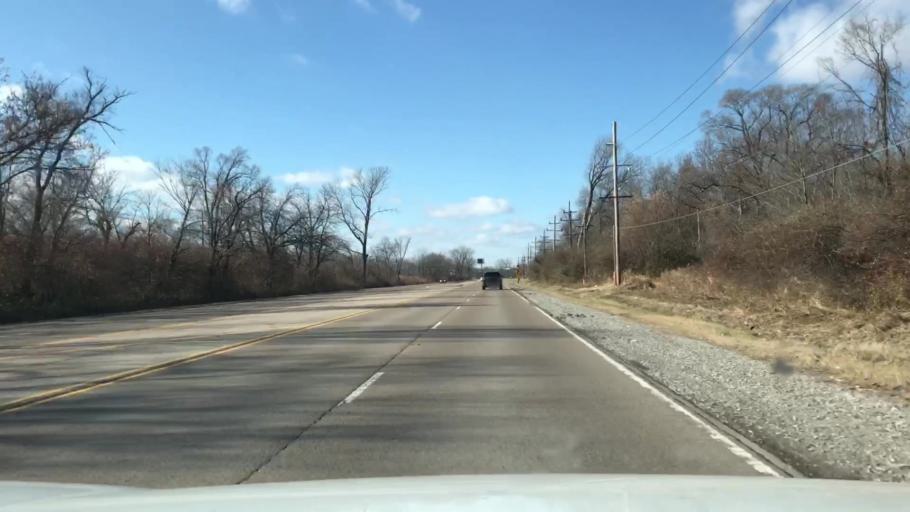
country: US
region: Illinois
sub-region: Saint Clair County
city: Washington Park
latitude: 38.6056
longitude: -90.0705
